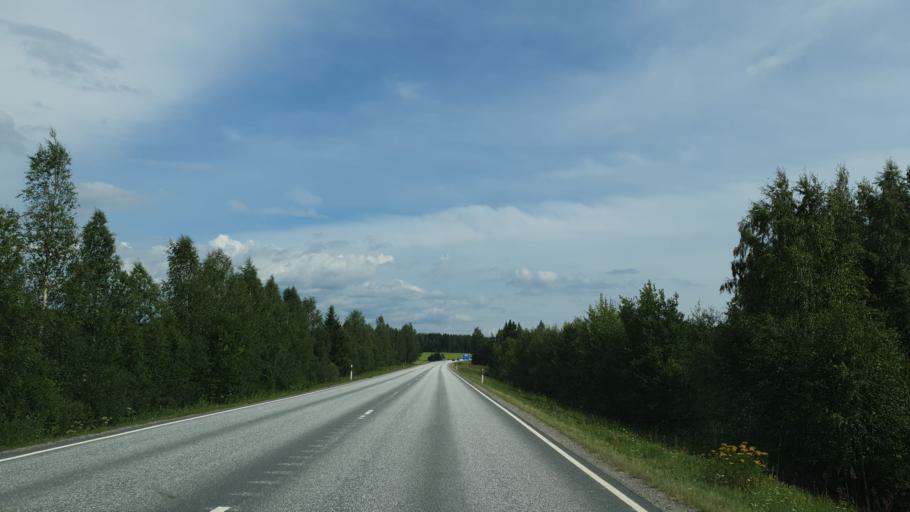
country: FI
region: North Karelia
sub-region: Pielisen Karjala
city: Nurmes
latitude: 63.5677
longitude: 28.9908
